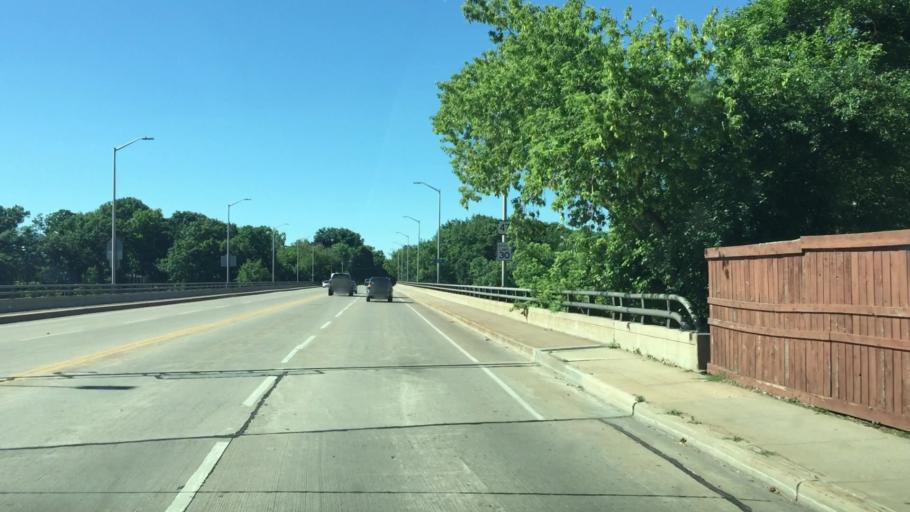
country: US
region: Wisconsin
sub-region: Outagamie County
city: Appleton
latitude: 44.2540
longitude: -88.4155
